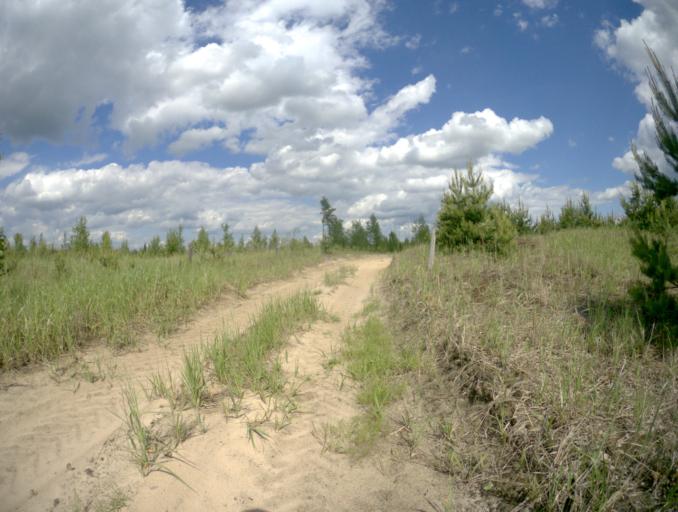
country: RU
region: Vladimir
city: Velikodvorskiy
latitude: 55.2736
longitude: 40.8686
